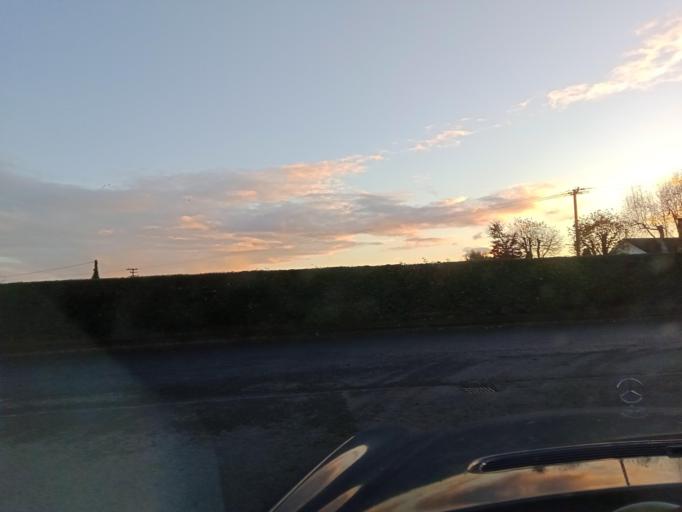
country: IE
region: Leinster
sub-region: Kilkenny
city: Kilkenny
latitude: 52.6013
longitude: -7.1927
